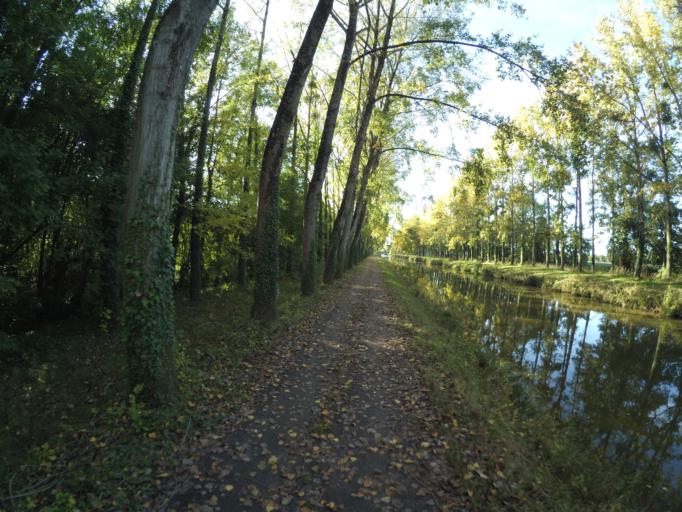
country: FR
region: Brittany
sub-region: Departement du Morbihan
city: Saint-Vincent-sur-Oust
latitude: 47.7216
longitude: -2.1769
